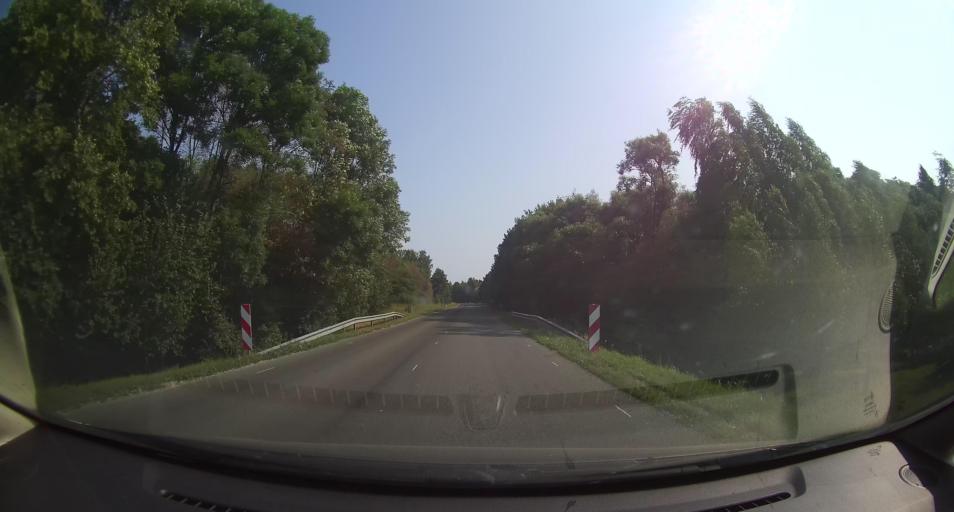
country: EE
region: Paernumaa
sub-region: Audru vald
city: Audru
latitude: 58.4701
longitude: 24.3203
